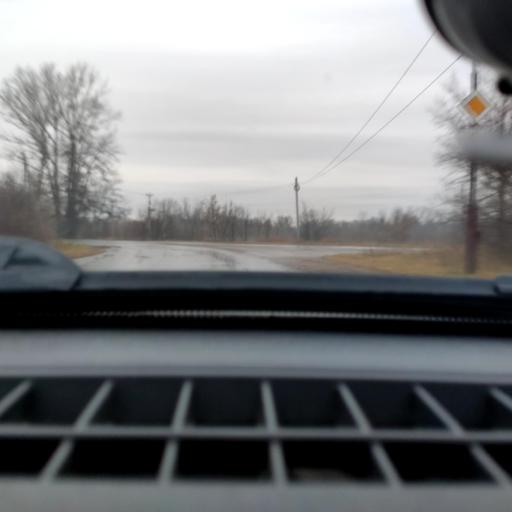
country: RU
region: Bashkortostan
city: Iglino
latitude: 54.7980
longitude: 56.2109
